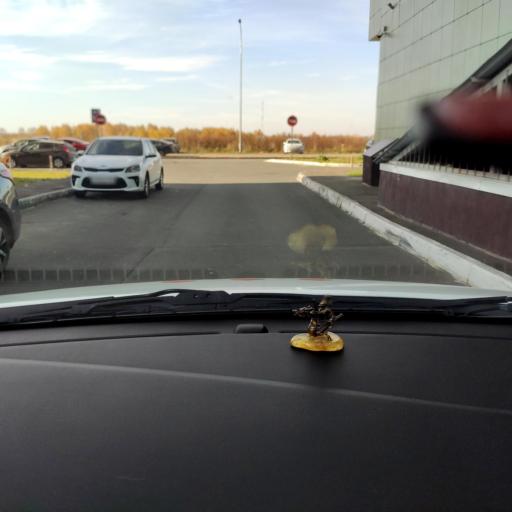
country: RU
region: Tatarstan
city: Osinovo
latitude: 55.8651
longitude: 48.8720
